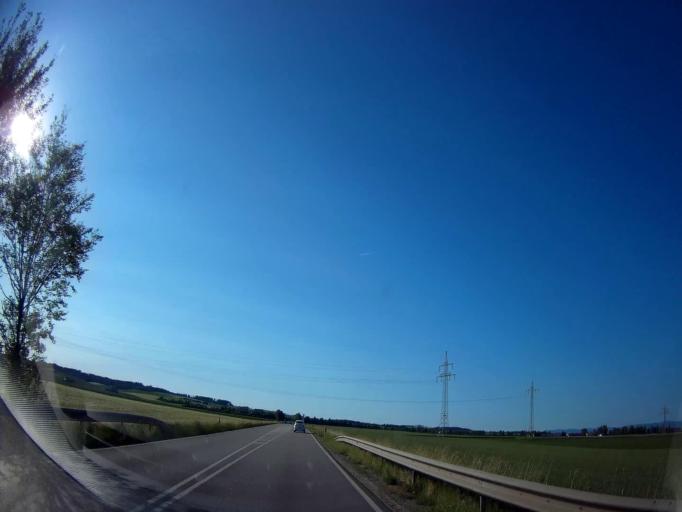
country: DE
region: Bavaria
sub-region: Lower Bavaria
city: Pilsting
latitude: 48.7197
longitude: 12.6682
